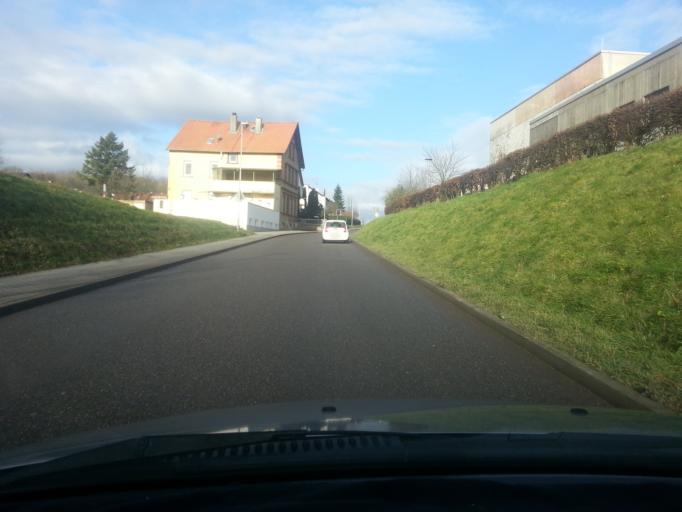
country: DE
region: Baden-Wuerttemberg
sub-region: Karlsruhe Region
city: Zaisenhausen
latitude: 49.1798
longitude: 8.8349
